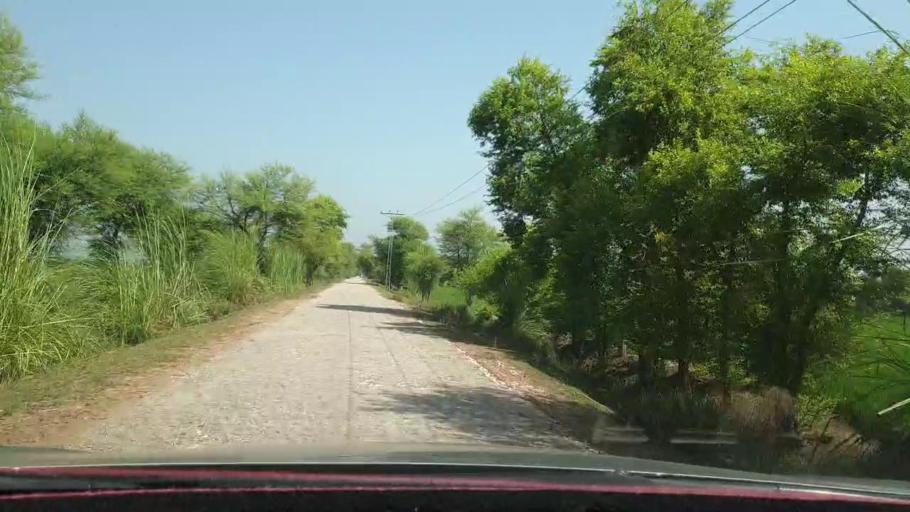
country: PK
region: Sindh
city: Warah
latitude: 27.4923
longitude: 67.8353
